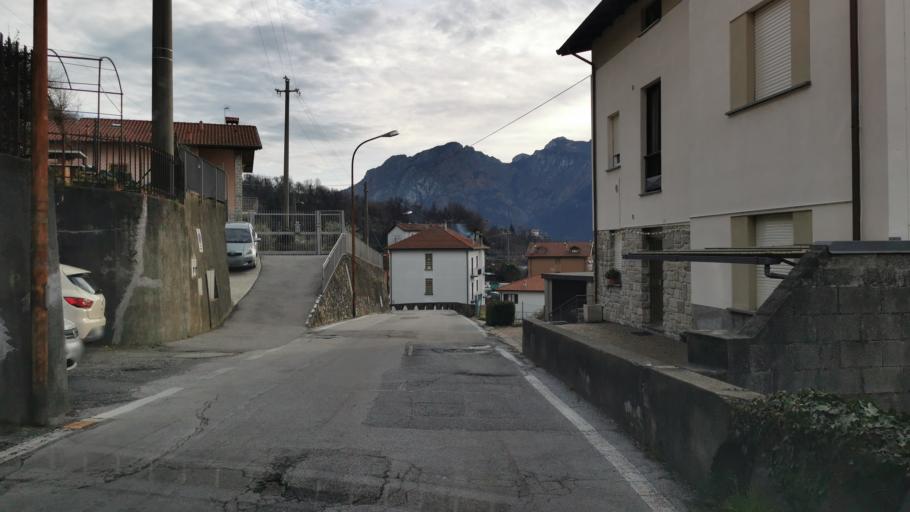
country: IT
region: Lombardy
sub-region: Provincia di Lecco
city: Mandello del Lario
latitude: 45.9236
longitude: 9.3271
